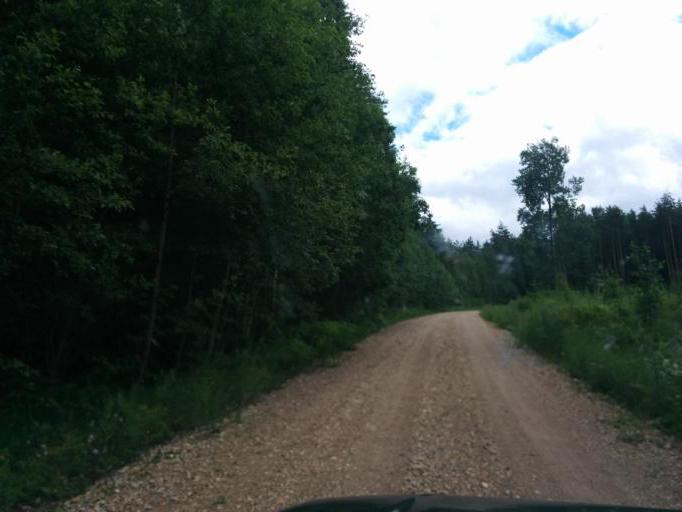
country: LV
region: Vilaka
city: Vilaka
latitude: 57.3770
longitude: 27.6275
